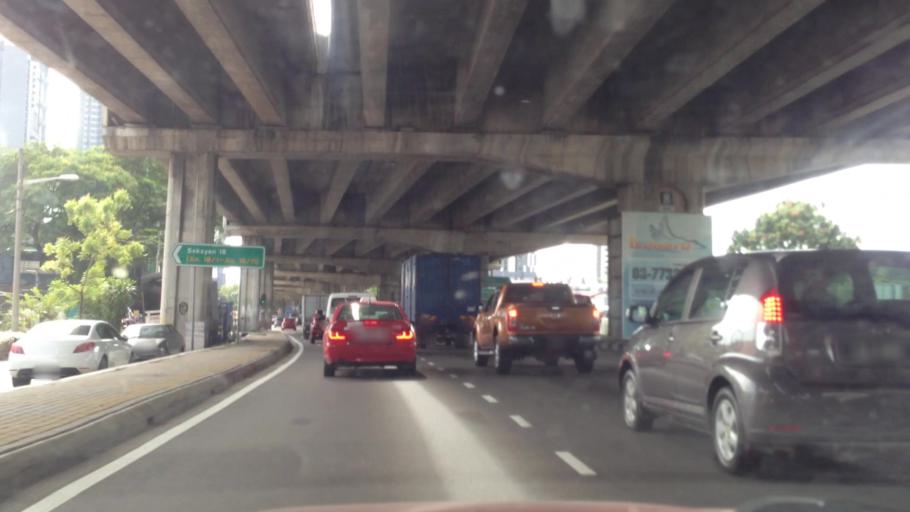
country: MY
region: Selangor
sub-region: Petaling
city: Petaling Jaya
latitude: 3.0817
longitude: 101.6567
